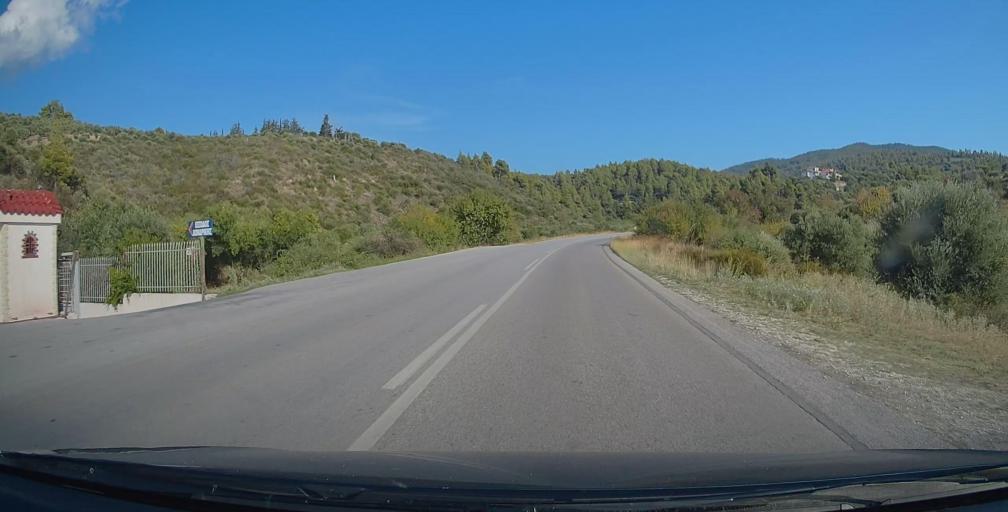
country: GR
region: Central Macedonia
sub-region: Nomos Chalkidikis
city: Neos Marmaras
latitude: 40.0854
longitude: 23.8070
